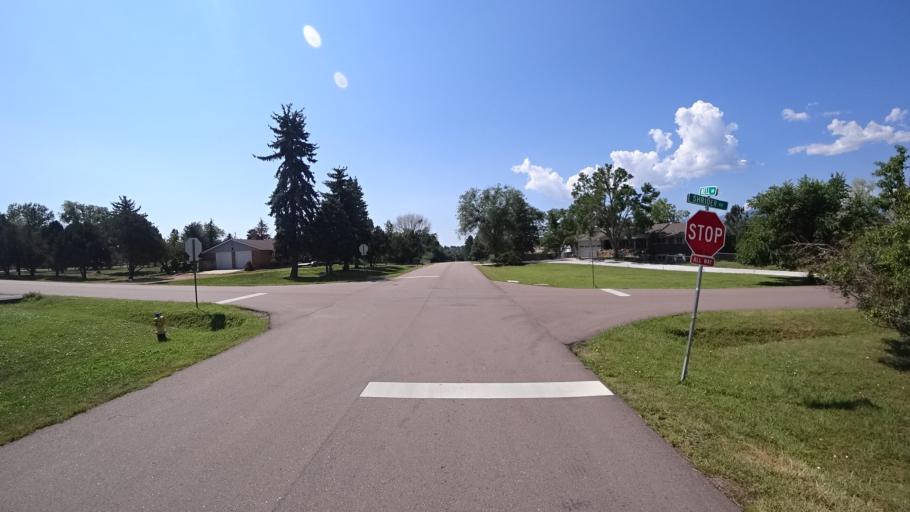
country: US
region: Colorado
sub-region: El Paso County
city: Air Force Academy
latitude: 38.9364
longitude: -104.7876
